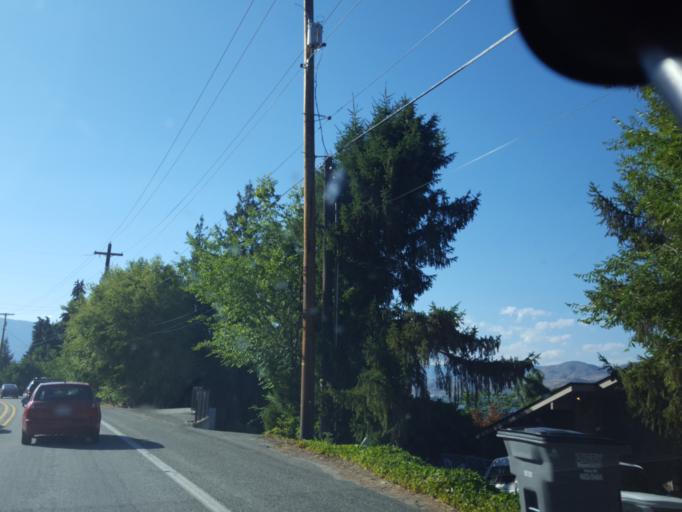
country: US
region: Washington
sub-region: Chelan County
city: Manson
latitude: 47.8440
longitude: -120.1032
